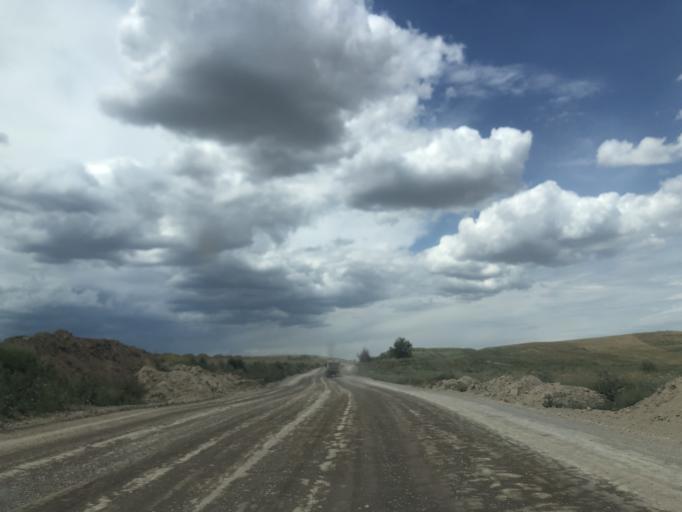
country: KG
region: Chuy
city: Bystrovka
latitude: 43.3217
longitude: 75.9846
